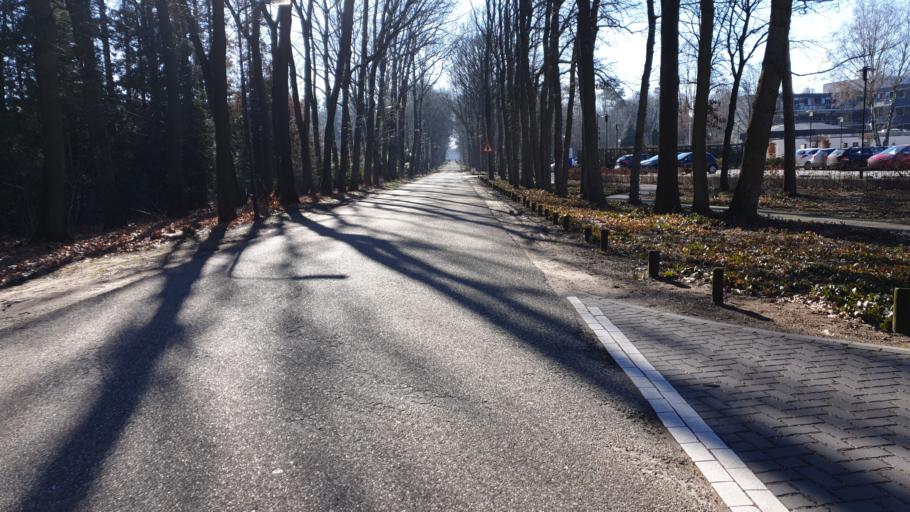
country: NL
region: Gelderland
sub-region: Gemeente Apeldoorn
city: Beekbergen
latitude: 52.1809
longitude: 5.9502
